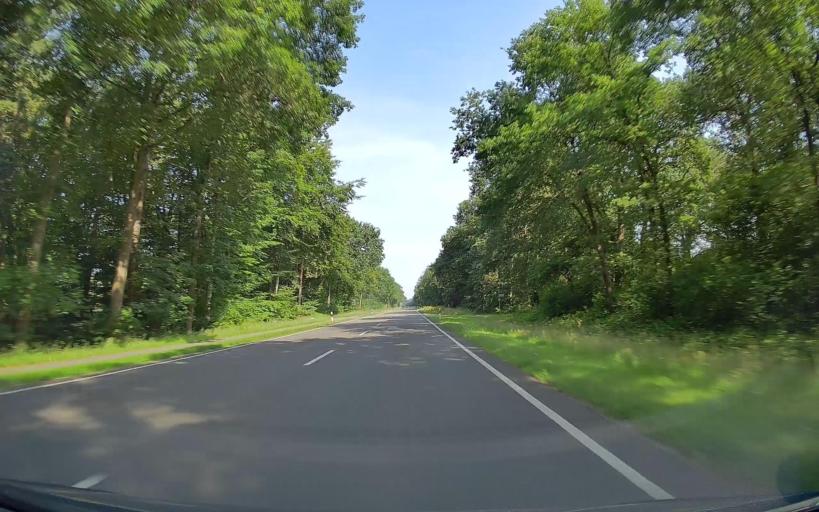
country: DE
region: Lower Saxony
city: Bosel
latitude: 52.9448
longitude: 7.9392
